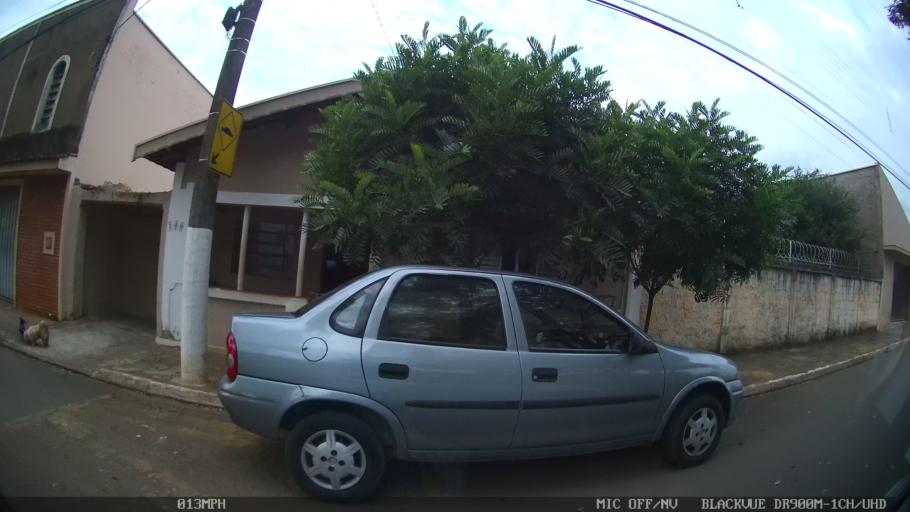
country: BR
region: Sao Paulo
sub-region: Americana
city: Americana
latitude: -22.6510
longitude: -47.3531
